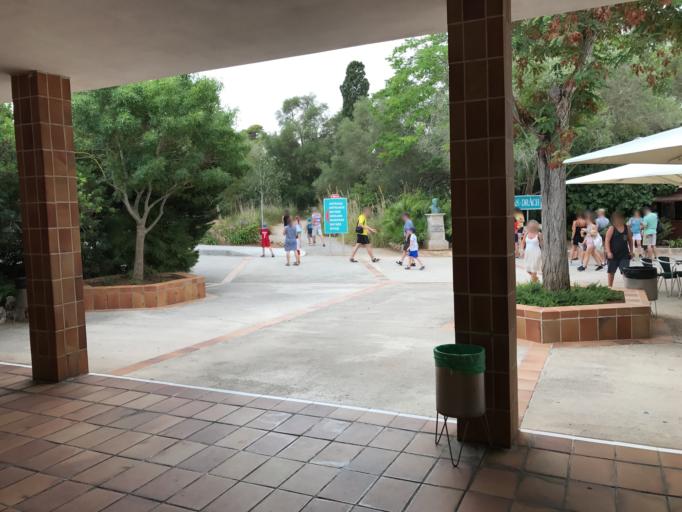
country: ES
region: Balearic Islands
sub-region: Illes Balears
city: Sant Llorenc des Cardassar
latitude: 39.5357
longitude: 3.3305
